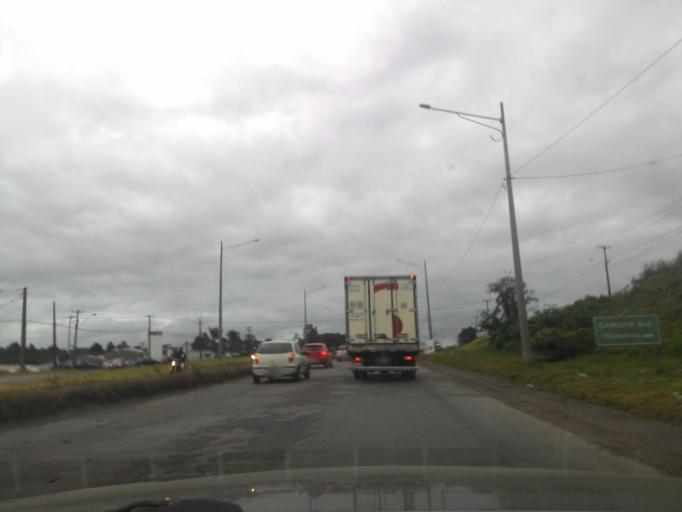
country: BR
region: Parana
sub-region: Sao Jose Dos Pinhais
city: Sao Jose dos Pinhais
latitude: -25.5358
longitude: -49.3012
